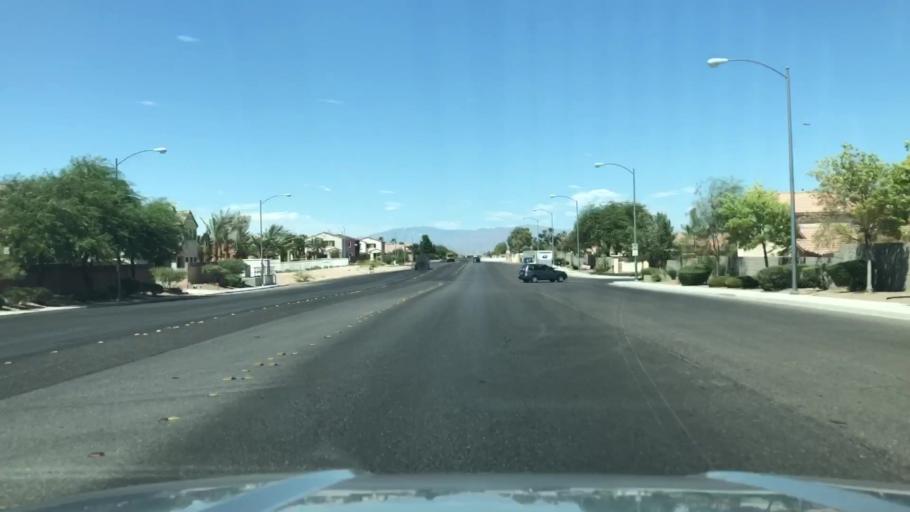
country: US
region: Nevada
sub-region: Clark County
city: Enterprise
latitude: 36.0445
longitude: -115.2078
